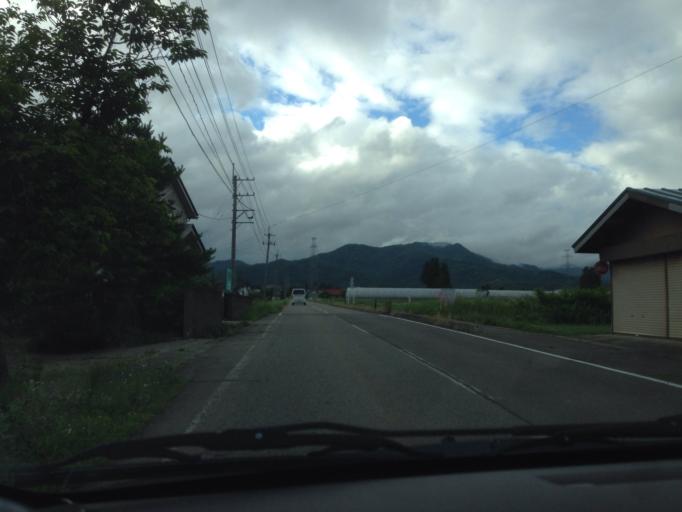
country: JP
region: Fukushima
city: Kitakata
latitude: 37.6997
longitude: 139.8577
